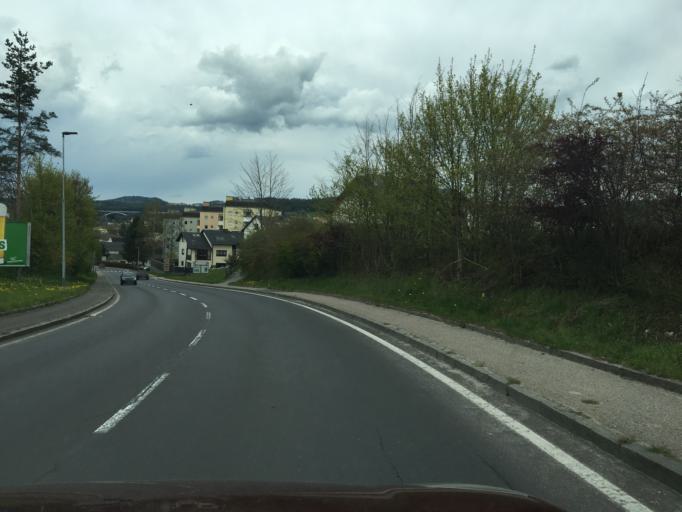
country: AT
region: Upper Austria
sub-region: Politischer Bezirk Freistadt
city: Freistadt
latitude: 48.4992
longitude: 14.4998
